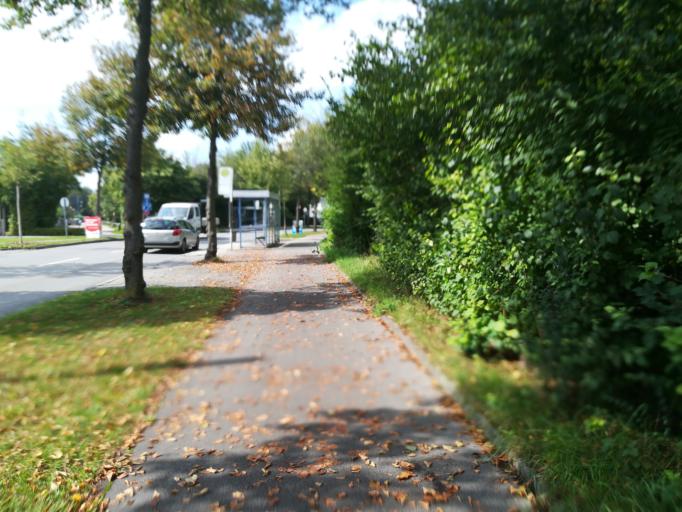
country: DE
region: Bavaria
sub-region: Upper Bavaria
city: Oberschleissheim
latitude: 48.2070
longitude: 11.5343
